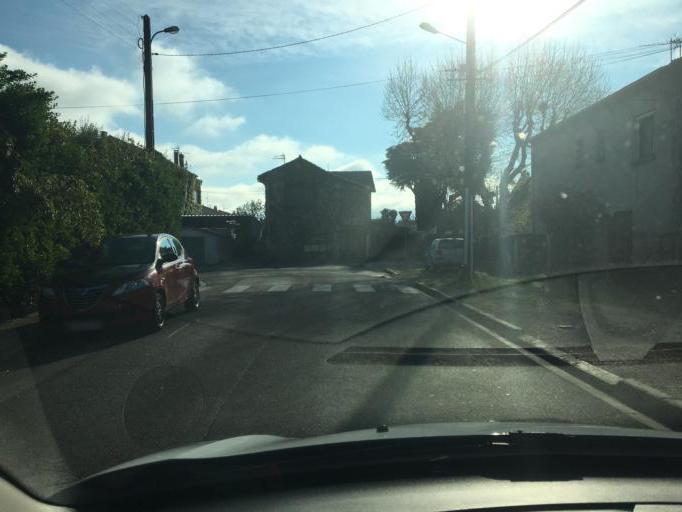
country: FR
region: Provence-Alpes-Cote d'Azur
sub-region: Departement du Vaucluse
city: Cavaillon
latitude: 43.8268
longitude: 5.0397
